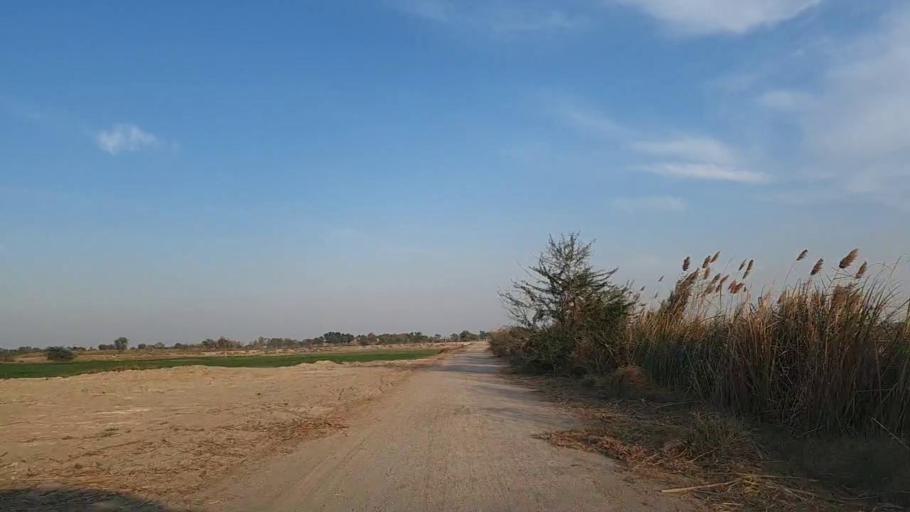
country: PK
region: Sindh
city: Bandhi
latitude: 26.5743
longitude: 68.3477
